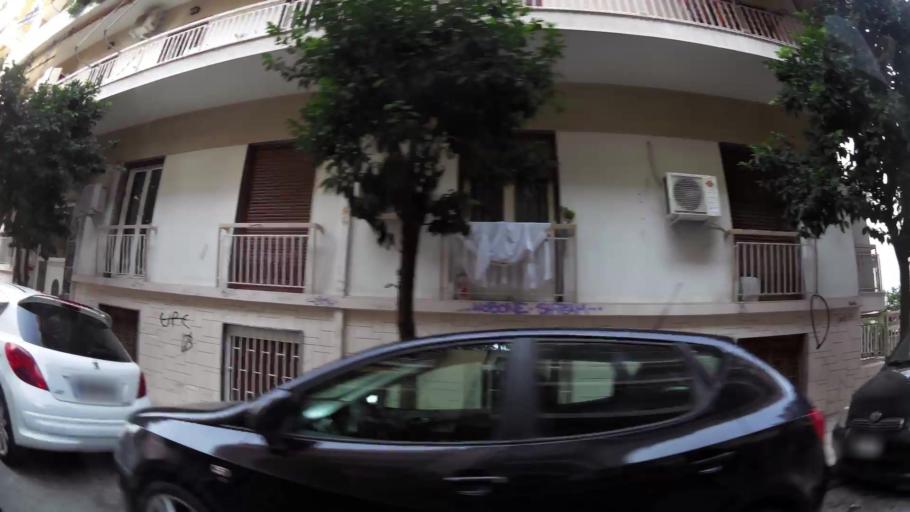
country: GR
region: Attica
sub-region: Nomarchia Athinas
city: Kallithea
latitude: 37.9559
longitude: 23.6992
